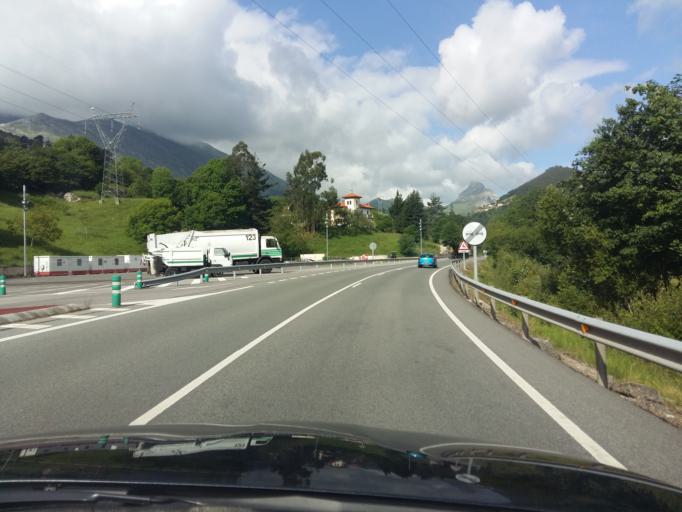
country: ES
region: Cantabria
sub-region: Provincia de Cantabria
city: Tresviso
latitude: 43.3200
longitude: -4.5930
